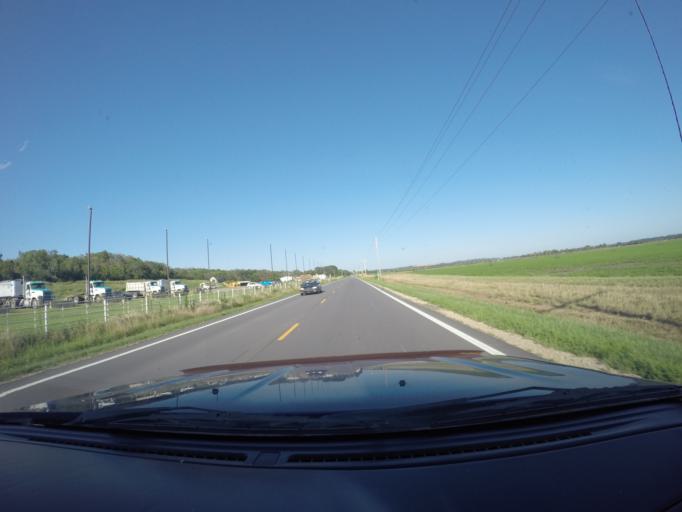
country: US
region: Kansas
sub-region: Douglas County
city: Lawrence
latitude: 39.0657
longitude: -95.3228
